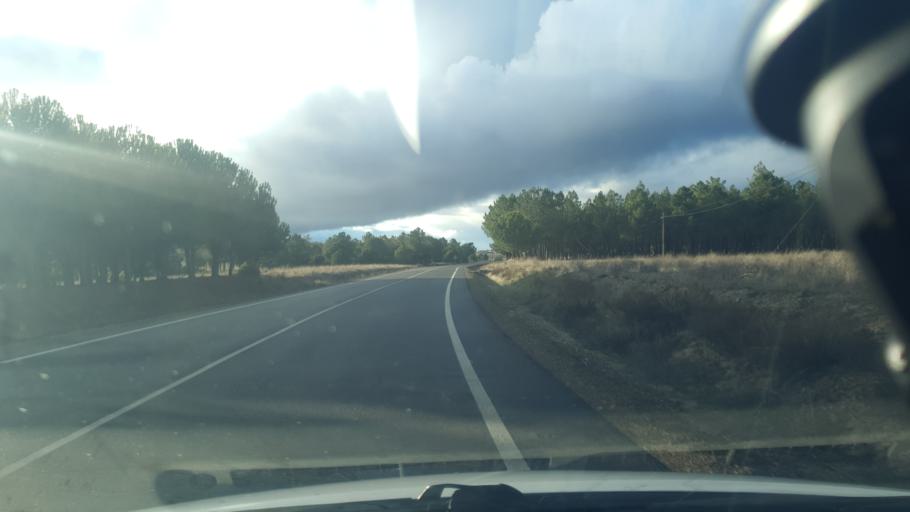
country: ES
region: Castille and Leon
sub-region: Provincia de Segovia
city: Santiuste de San Juan Bautista
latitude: 41.1492
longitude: -4.5450
